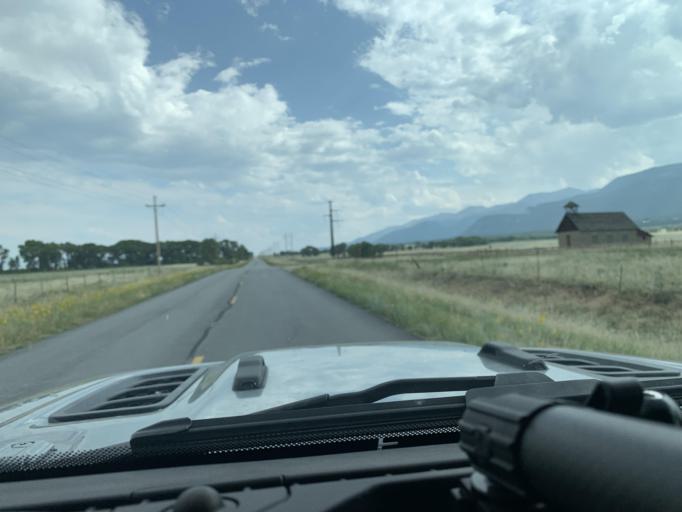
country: US
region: Colorado
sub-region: Chaffee County
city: Buena Vista
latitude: 38.7969
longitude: -106.1465
